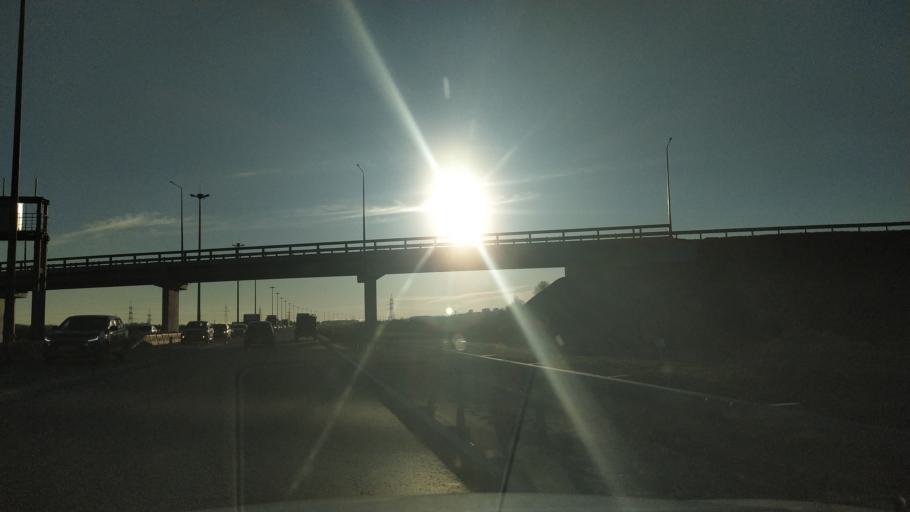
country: RU
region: Leningrad
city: Parnas
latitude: 60.0951
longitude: 30.3345
